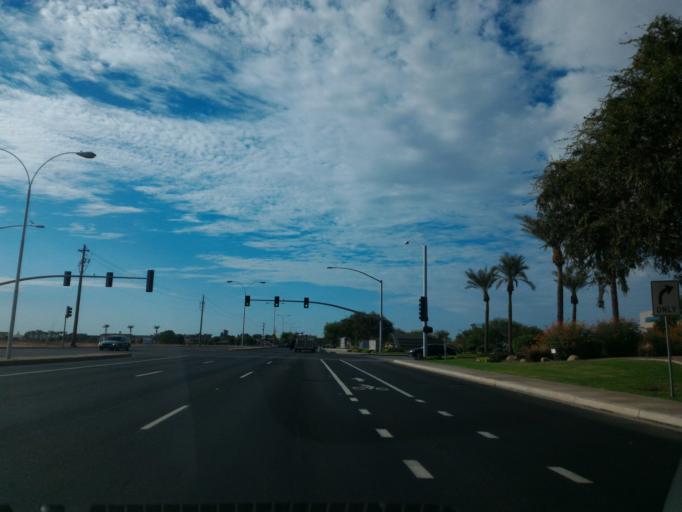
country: US
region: Arizona
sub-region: Maricopa County
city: Sun Lakes
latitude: 33.2657
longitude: -111.8889
